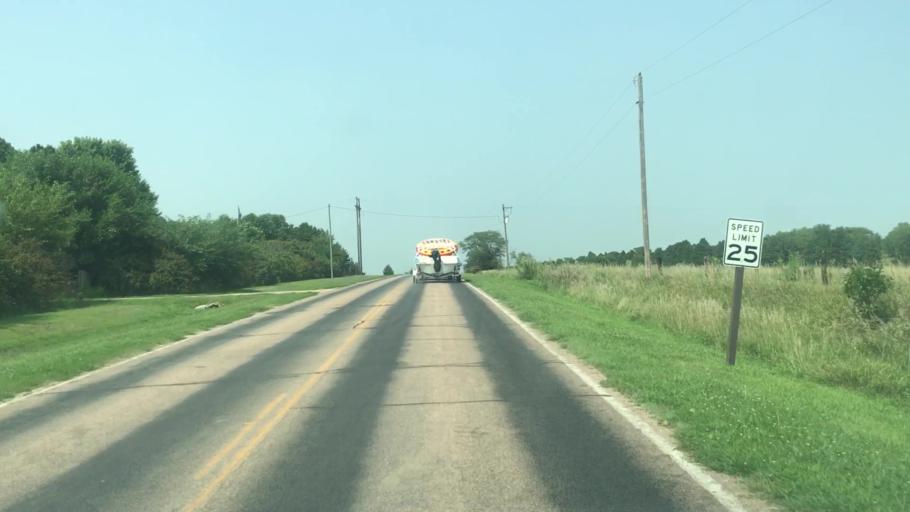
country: US
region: Nebraska
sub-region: Sherman County
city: Loup City
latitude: 41.2850
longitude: -98.8998
